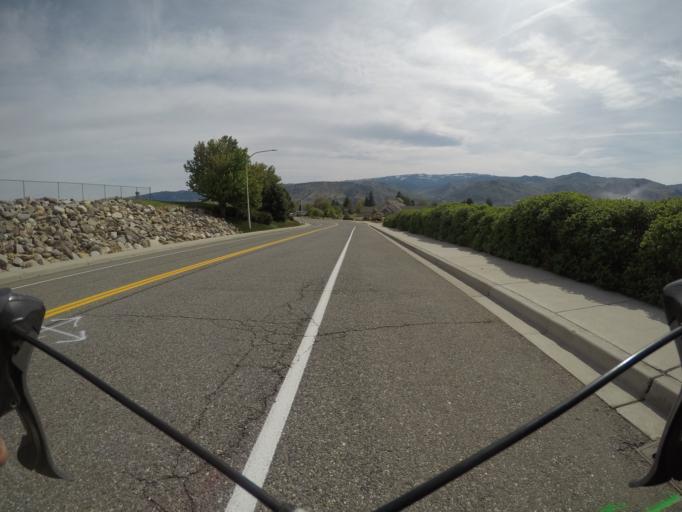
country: US
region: Washington
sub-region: Douglas County
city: East Wenatchee Bench
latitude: 47.4191
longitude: -120.2762
